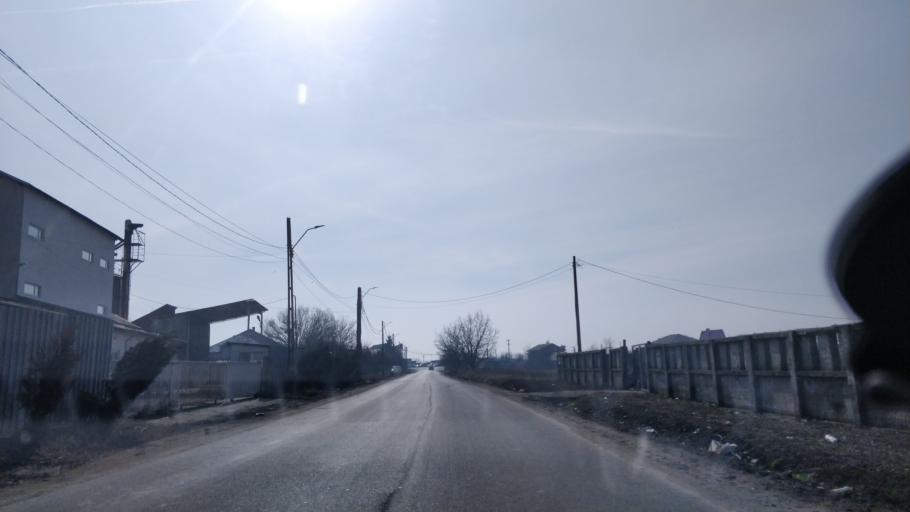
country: RO
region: Giurgiu
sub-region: Comuna Bolintin Vale
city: Bolintin Vale
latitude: 44.4512
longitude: 25.7793
